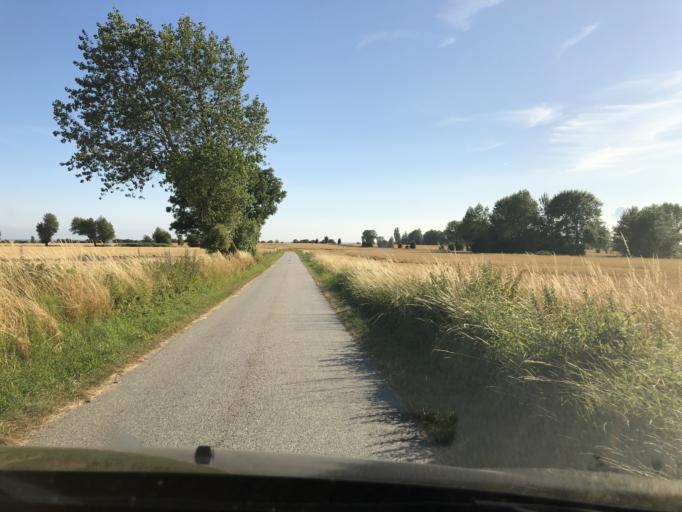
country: DK
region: South Denmark
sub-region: AEro Kommune
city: AEroskobing
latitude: 54.8556
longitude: 10.3786
